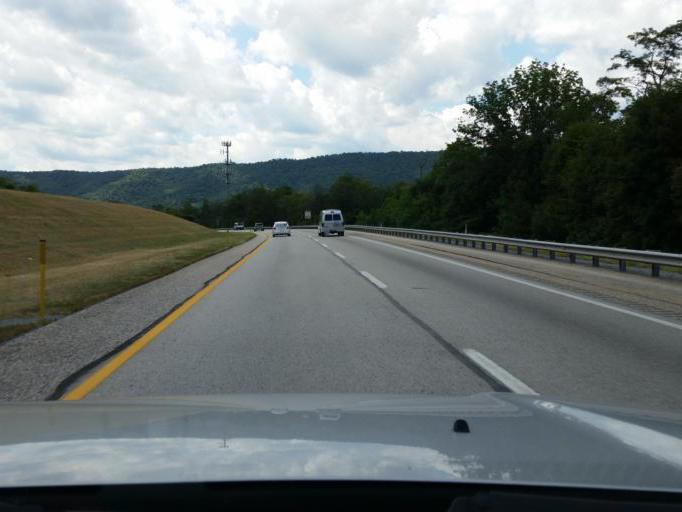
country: US
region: Pennsylvania
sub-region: Franklin County
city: Doylestown
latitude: 40.1591
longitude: -77.6832
